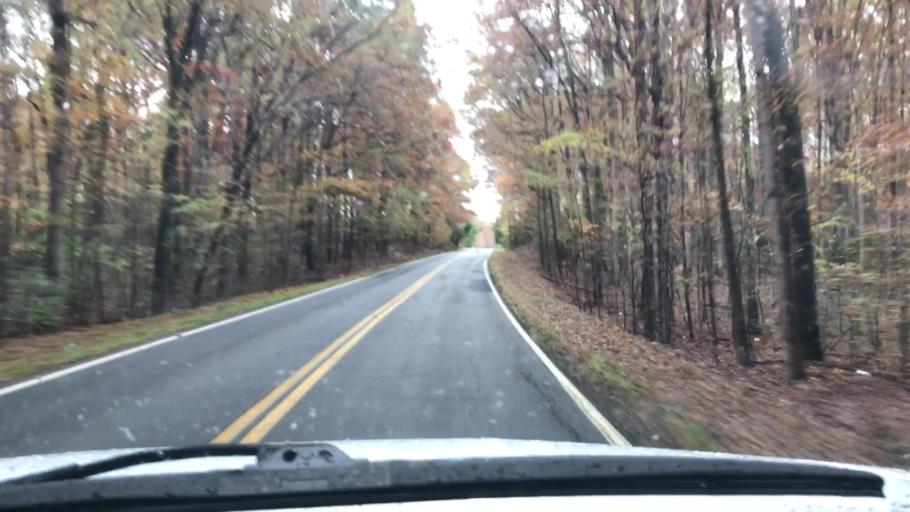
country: US
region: Virginia
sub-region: Henrico County
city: Short Pump
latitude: 37.6172
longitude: -77.6959
